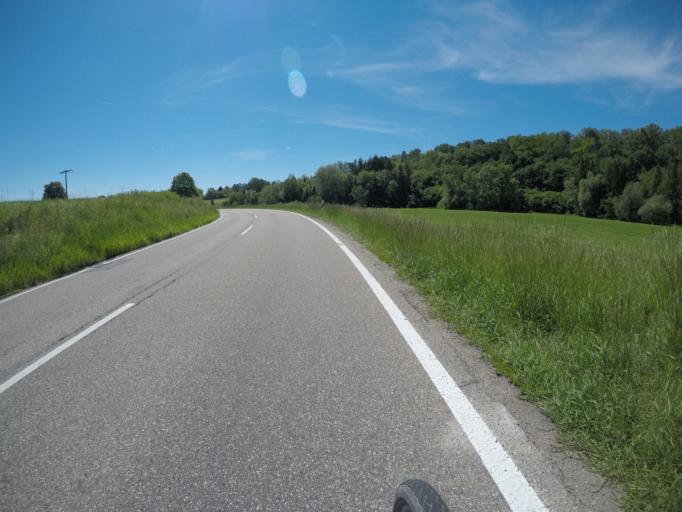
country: DE
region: Baden-Wuerttemberg
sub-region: Karlsruhe Region
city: Friolzheim
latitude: 48.7988
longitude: 8.8303
